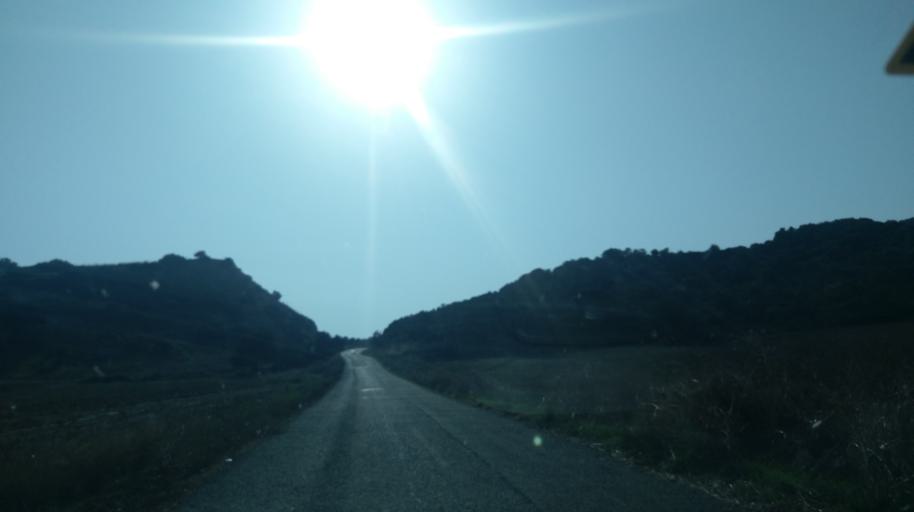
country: CY
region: Ammochostos
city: Rizokarpaso
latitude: 35.5283
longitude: 34.3277
